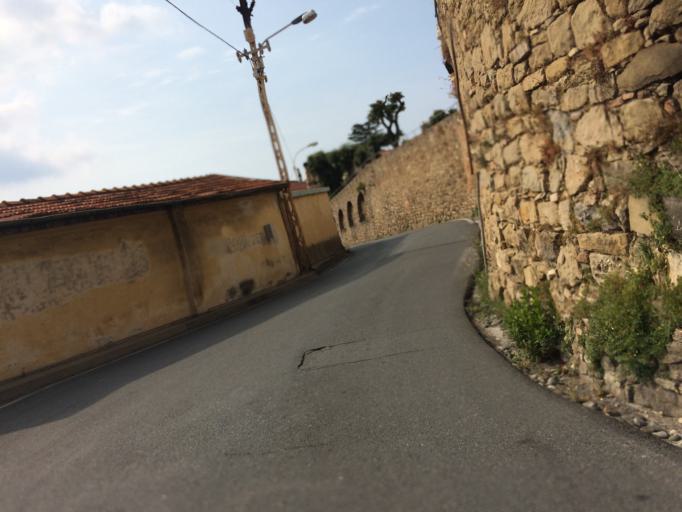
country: IT
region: Liguria
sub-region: Provincia di Imperia
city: San Remo
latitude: 43.8217
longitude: 7.7732
